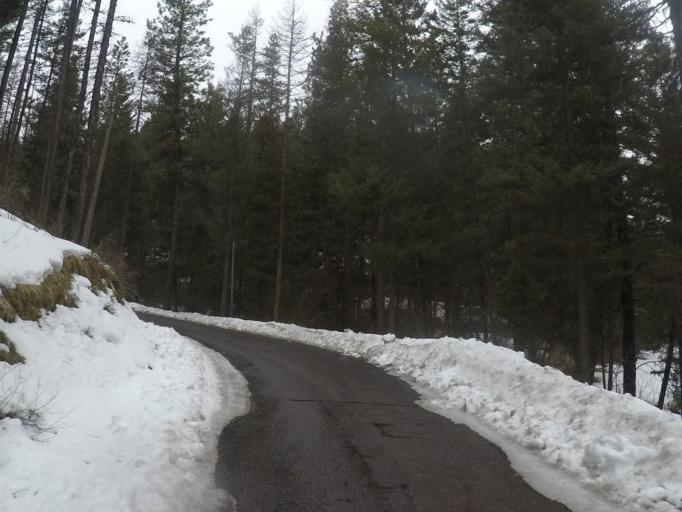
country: US
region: Montana
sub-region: Missoula County
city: Missoula
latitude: 46.9326
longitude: -113.9773
